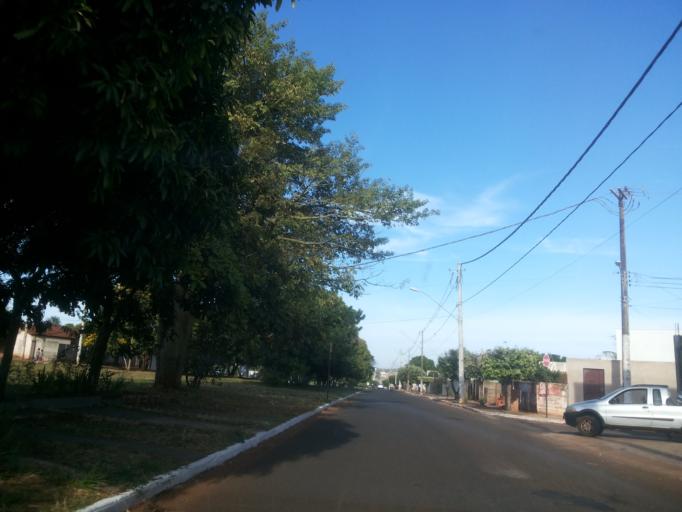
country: BR
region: Minas Gerais
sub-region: Ituiutaba
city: Ituiutaba
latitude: -18.9908
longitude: -49.4641
